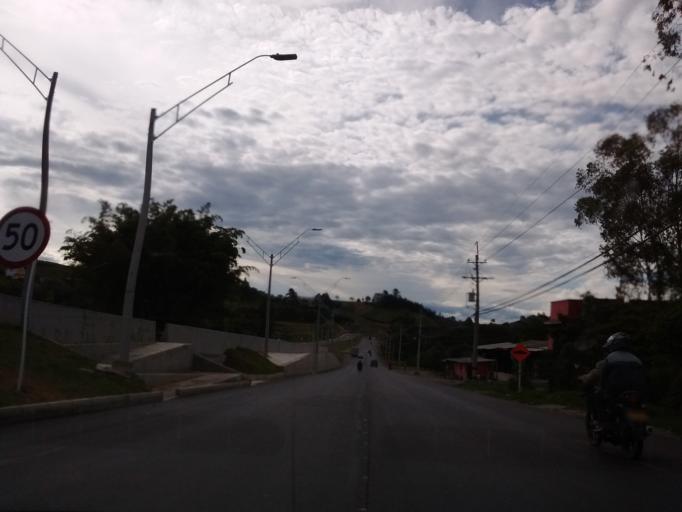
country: CO
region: Antioquia
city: Marinilla
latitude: 6.1559
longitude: -75.3147
